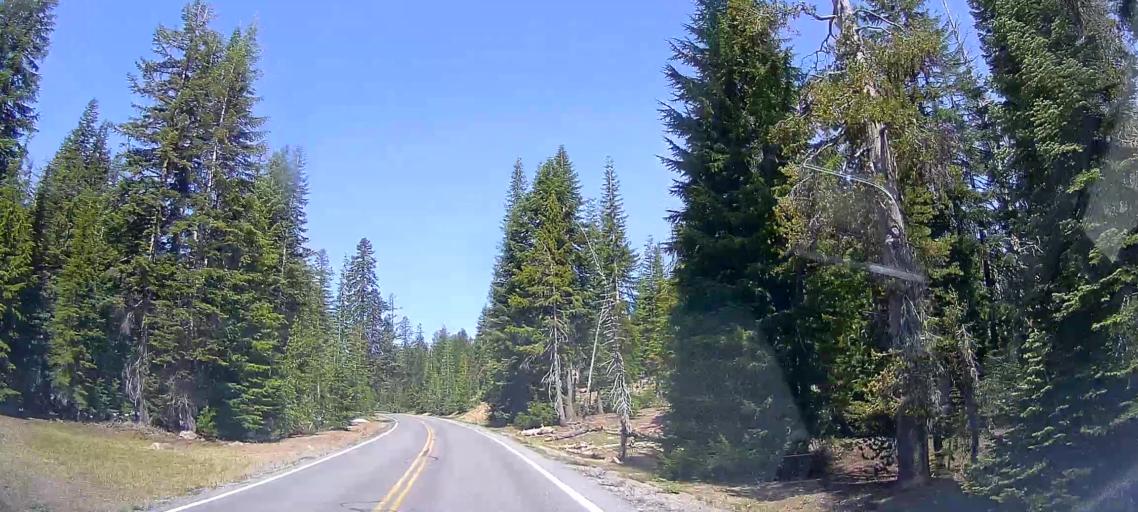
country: US
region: Oregon
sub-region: Klamath County
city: Klamath Falls
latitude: 42.8790
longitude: -122.1104
